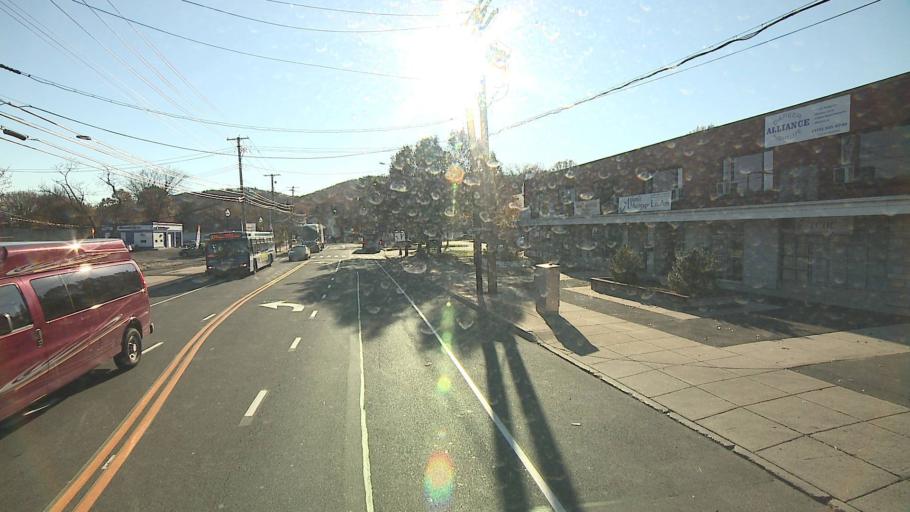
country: US
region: Connecticut
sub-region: New Haven County
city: New Haven
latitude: 41.3352
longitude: -72.9003
